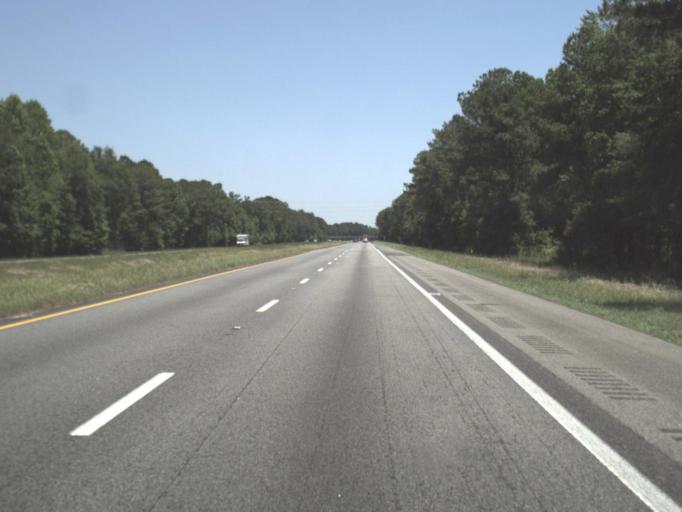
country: US
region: Florida
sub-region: Jefferson County
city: Monticello
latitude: 30.4726
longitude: -83.8367
